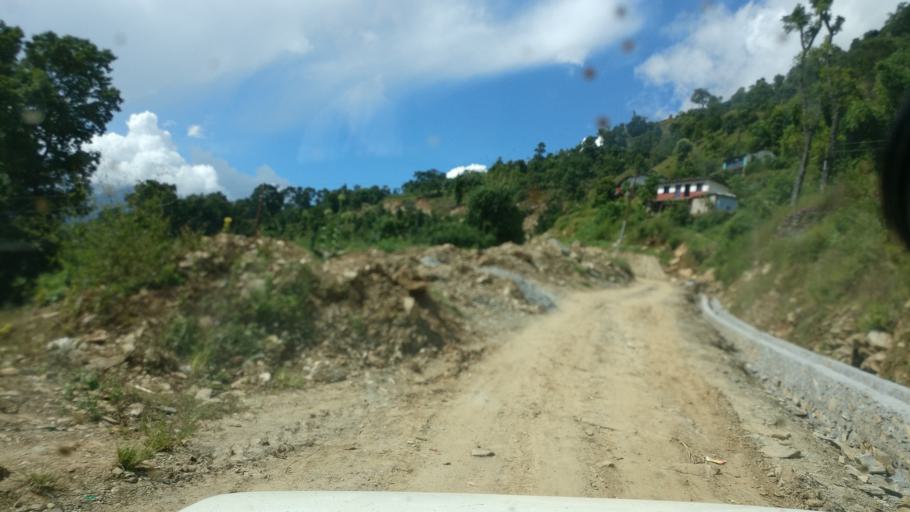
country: NP
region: Western Region
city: Baglung
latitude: 28.2613
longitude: 83.6435
